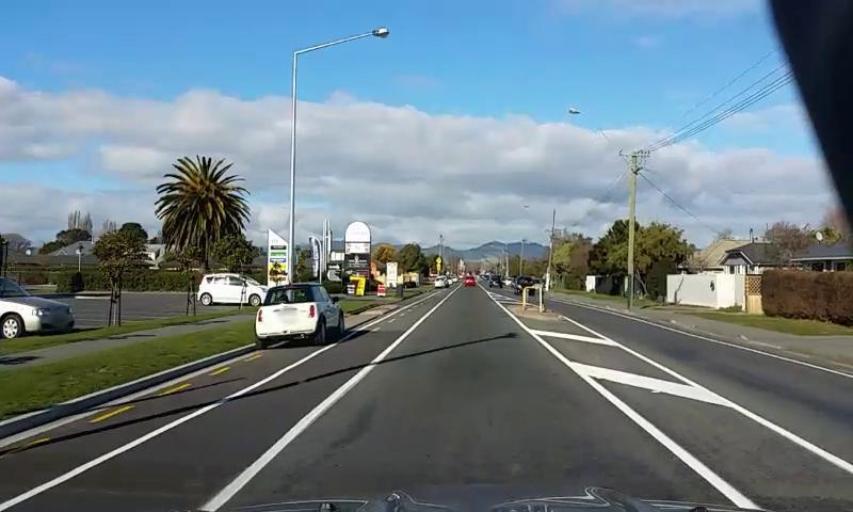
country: NZ
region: Canterbury
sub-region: Christchurch City
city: Christchurch
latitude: -43.4993
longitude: 172.6620
